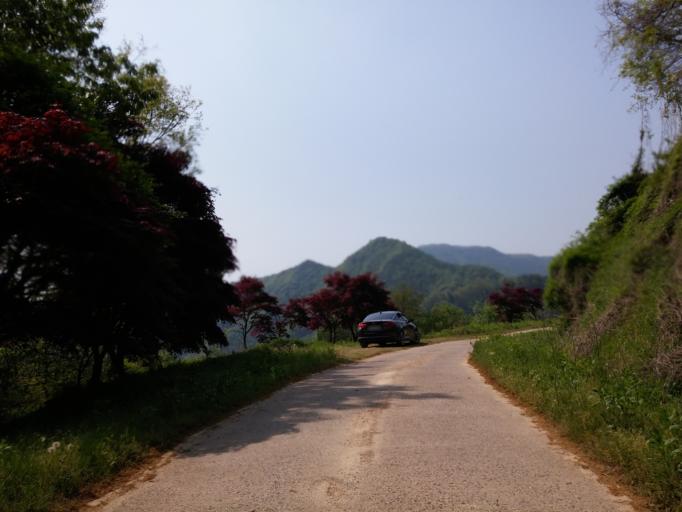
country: KR
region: Chungcheongbuk-do
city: Okcheon
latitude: 36.3825
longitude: 127.6048
